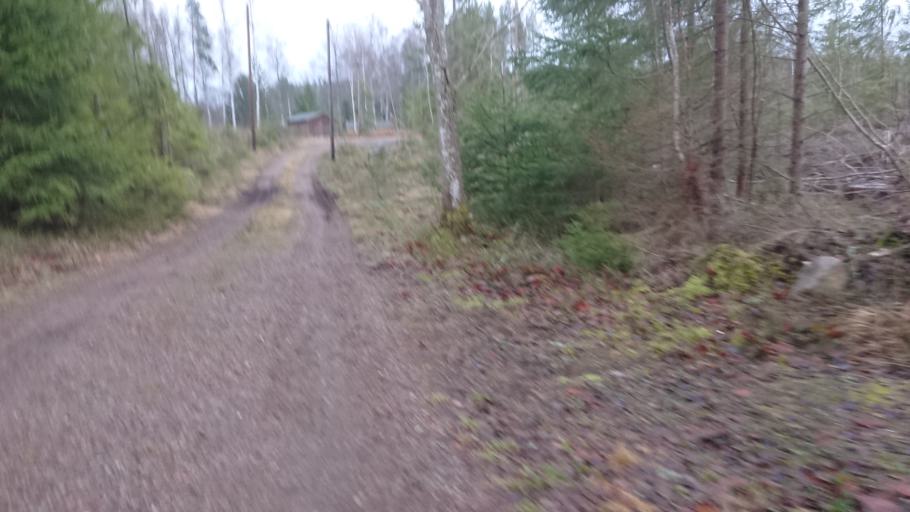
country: SE
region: Uppsala
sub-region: Osthammars Kommun
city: Bjorklinge
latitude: 60.0240
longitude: 17.5755
